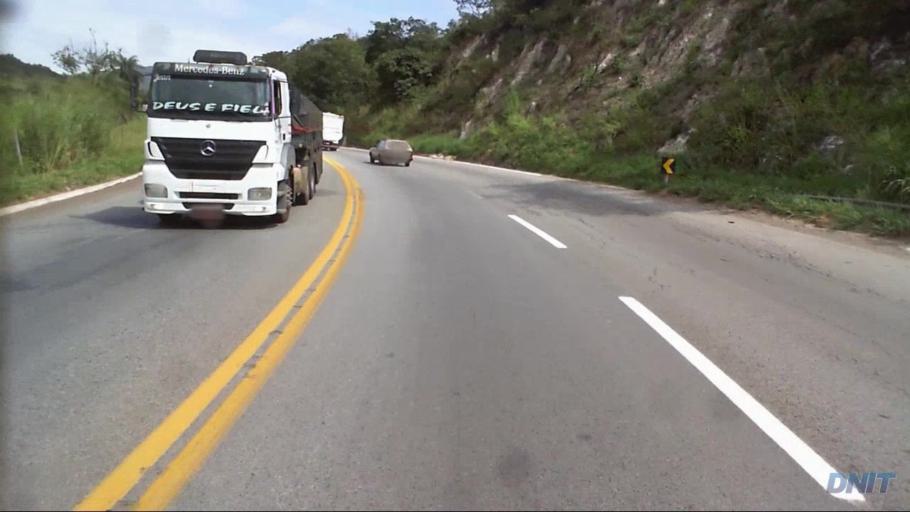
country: BR
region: Minas Gerais
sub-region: Santa Luzia
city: Santa Luzia
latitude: -19.7996
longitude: -43.7616
